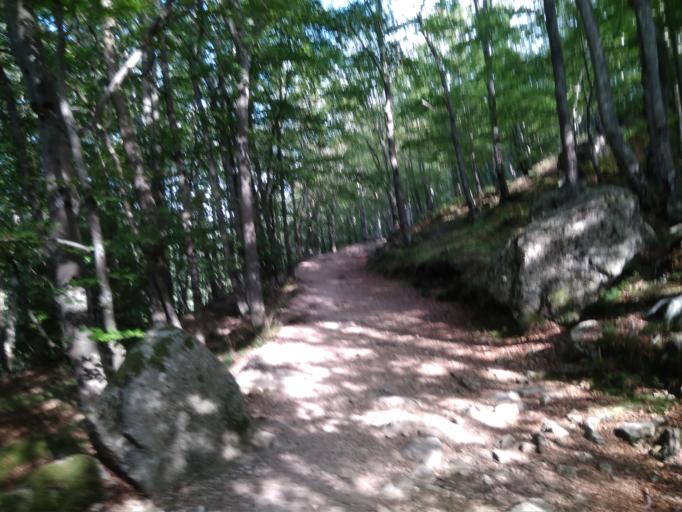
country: FR
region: Auvergne
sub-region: Departement de l'Allier
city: Le Mayet-de-Montagne
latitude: 46.1234
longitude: 3.7637
